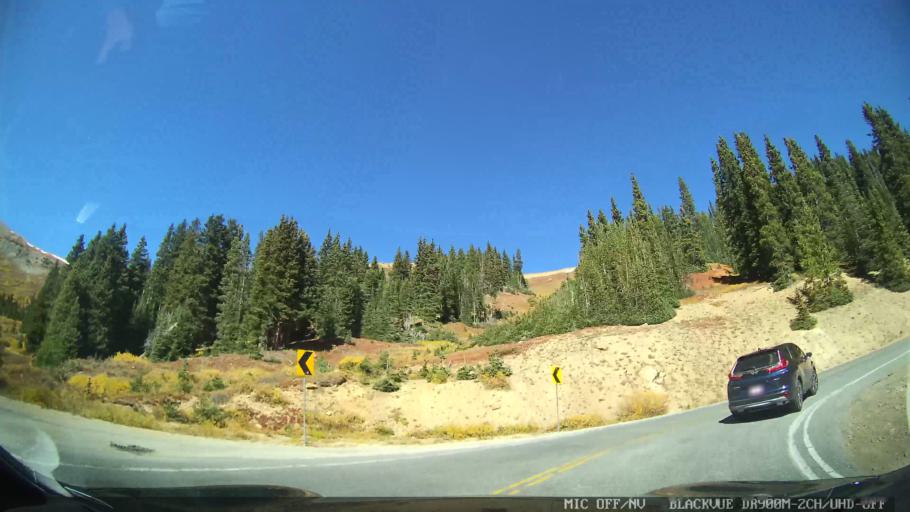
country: US
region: Colorado
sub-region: Pitkin County
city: Aspen
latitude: 39.0996
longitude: -106.5719
